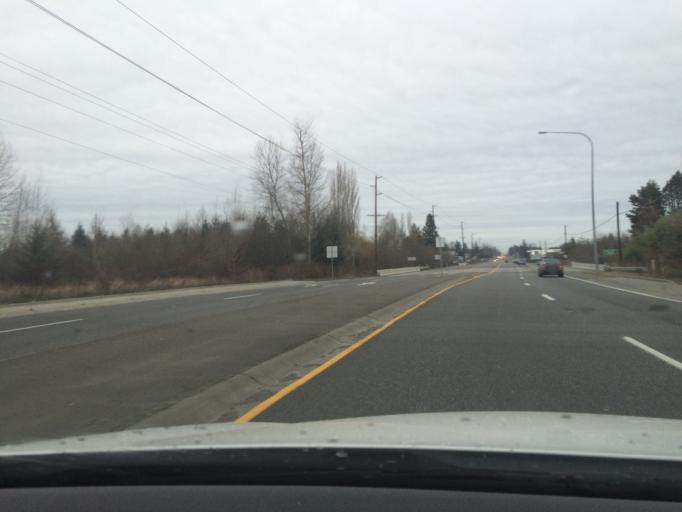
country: US
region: Washington
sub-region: Whatcom County
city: Lynden
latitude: 48.8692
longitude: -122.4860
